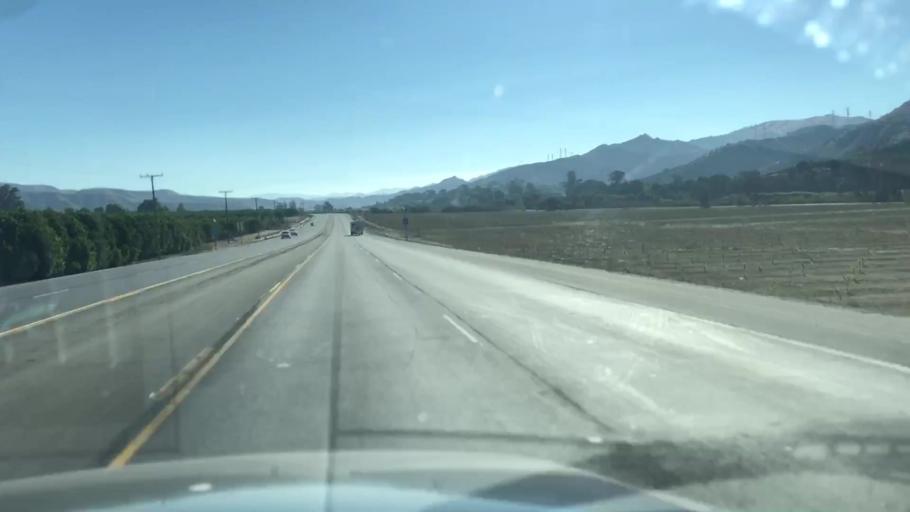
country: US
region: California
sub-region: Ventura County
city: Piru
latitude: 34.4064
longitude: -118.7526
